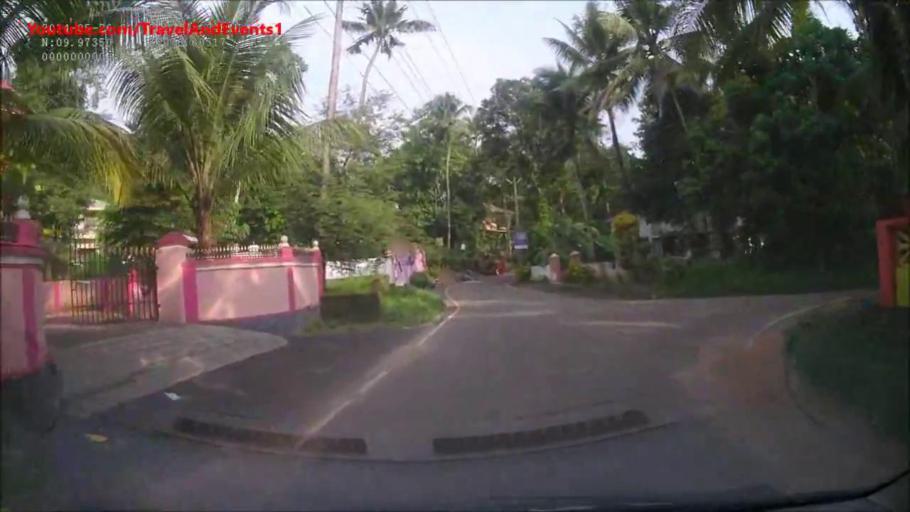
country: IN
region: Kerala
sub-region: Ernakulam
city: Muvattupula
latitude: 9.9669
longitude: 76.6123
